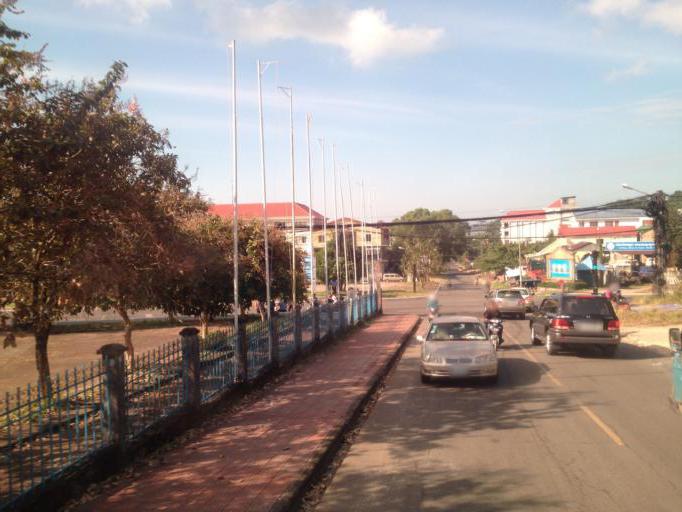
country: KH
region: Preah Sihanouk
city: Sihanoukville
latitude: 10.6311
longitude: 103.5060
